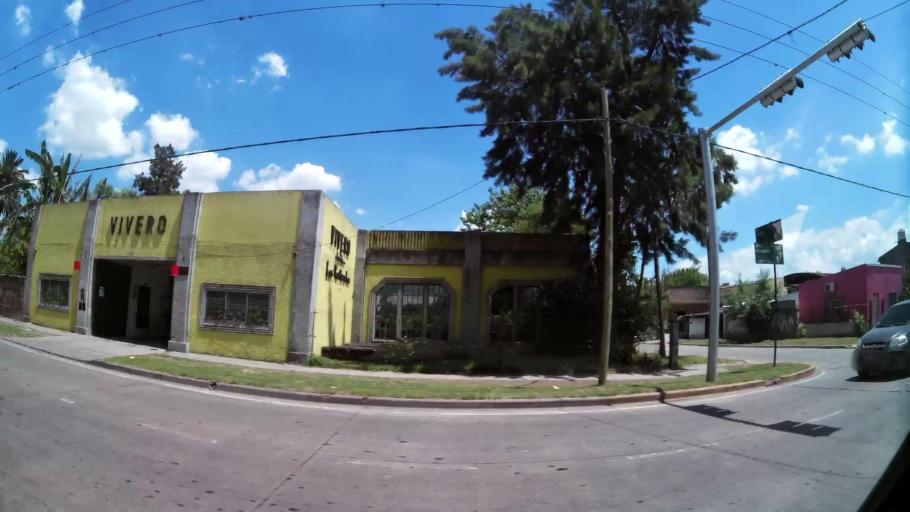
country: AR
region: Buenos Aires
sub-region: Partido de Tigre
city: Tigre
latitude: -34.4378
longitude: -58.5950
